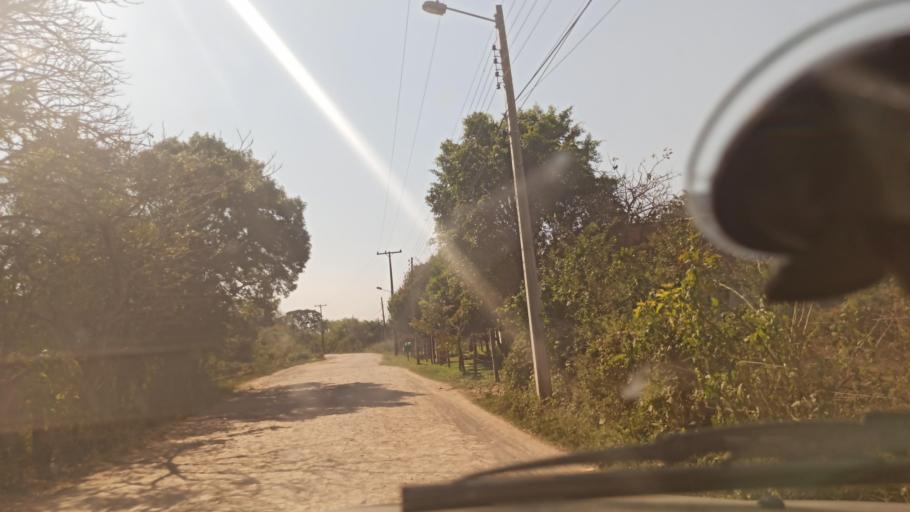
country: AR
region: Formosa
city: Clorinda
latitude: -25.2871
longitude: -57.6942
